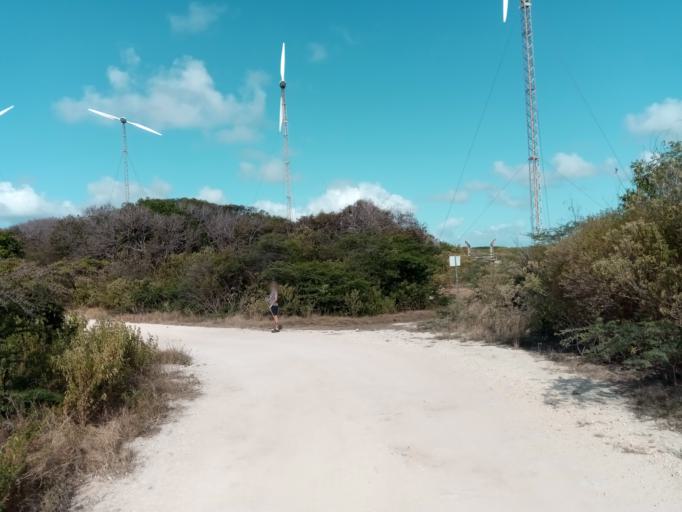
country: GP
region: Guadeloupe
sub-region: Guadeloupe
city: Saint-Francois
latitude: 16.2681
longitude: -61.2372
